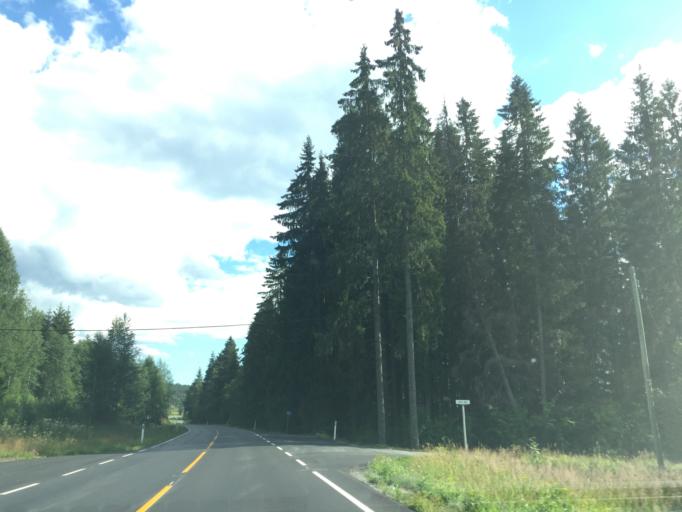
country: NO
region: Hedmark
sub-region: Sor-Odal
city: Skarnes
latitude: 60.2327
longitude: 11.6776
